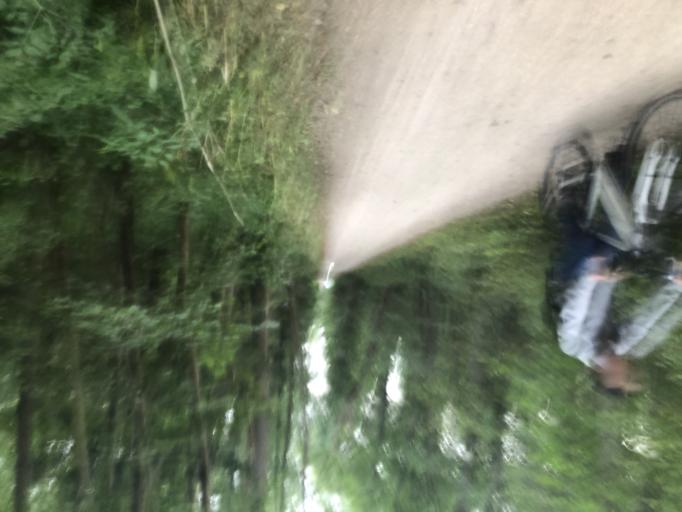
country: DE
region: Bavaria
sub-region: Regierungsbezirk Mittelfranken
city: Erlangen
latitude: 49.5650
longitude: 11.0213
